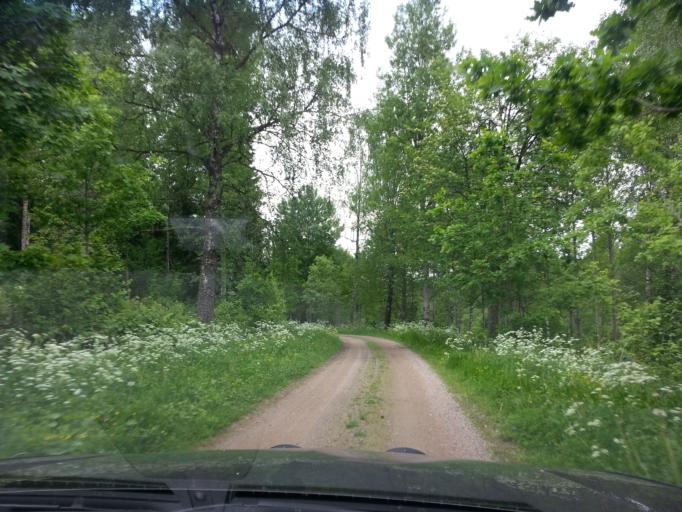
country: SE
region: Joenkoeping
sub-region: Vetlanda Kommun
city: Vetlanda
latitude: 57.2806
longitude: 15.1289
